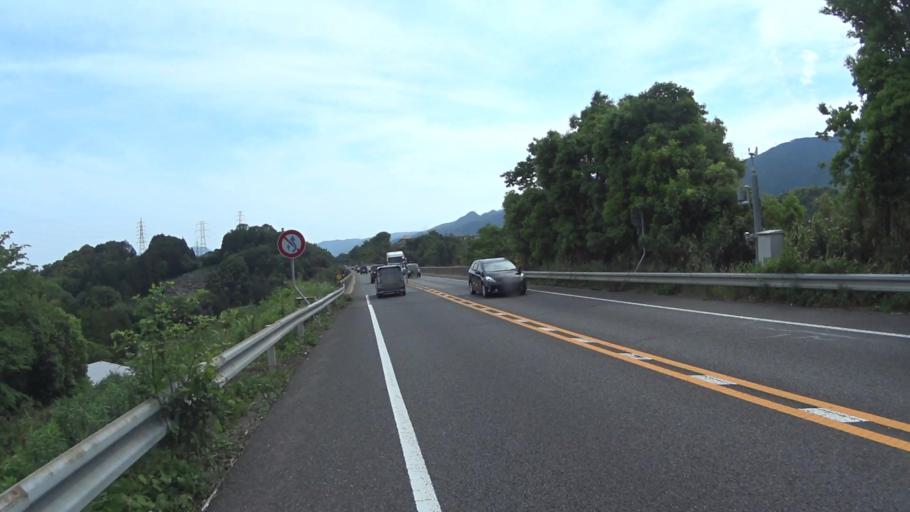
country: JP
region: Shiga Prefecture
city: Kitahama
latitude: 35.0875
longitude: 135.8863
